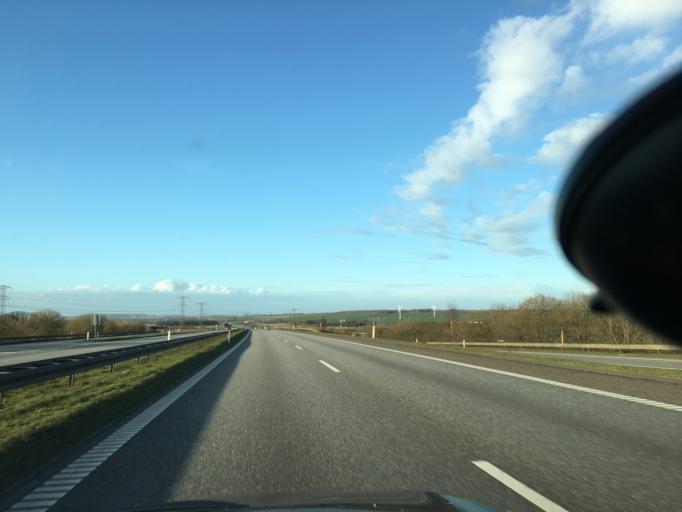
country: DK
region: North Denmark
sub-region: Alborg Kommune
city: Svenstrup
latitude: 56.9464
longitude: 9.8626
